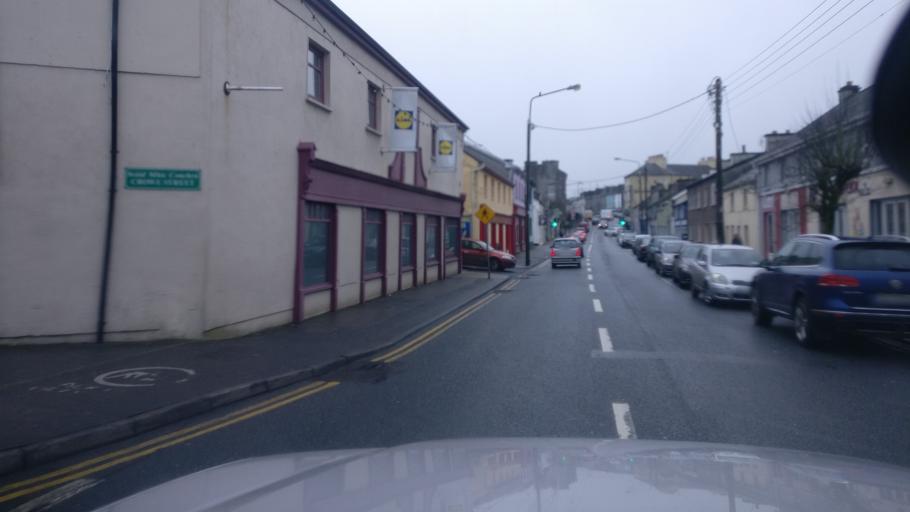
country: IE
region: Connaught
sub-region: County Galway
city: Gort
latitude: 53.0688
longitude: -8.8202
